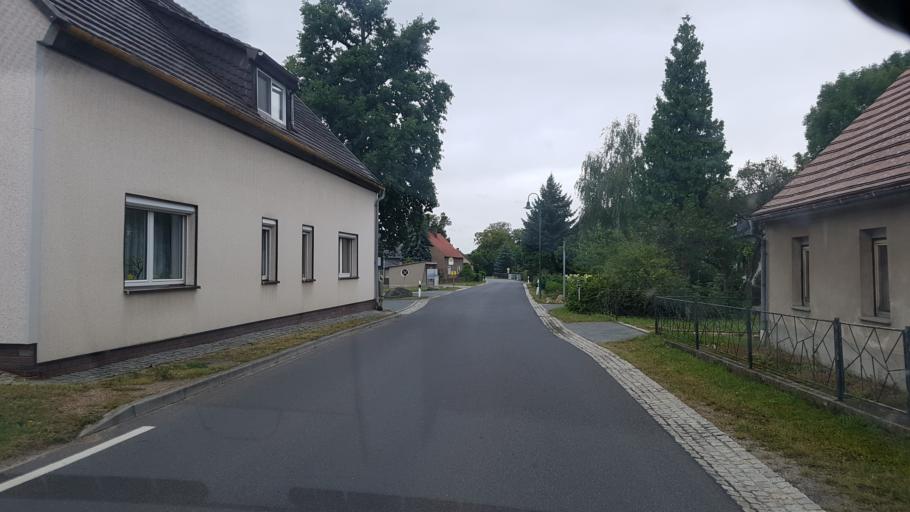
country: DE
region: Saxony
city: Kodersdorf
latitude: 51.2264
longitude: 14.8596
